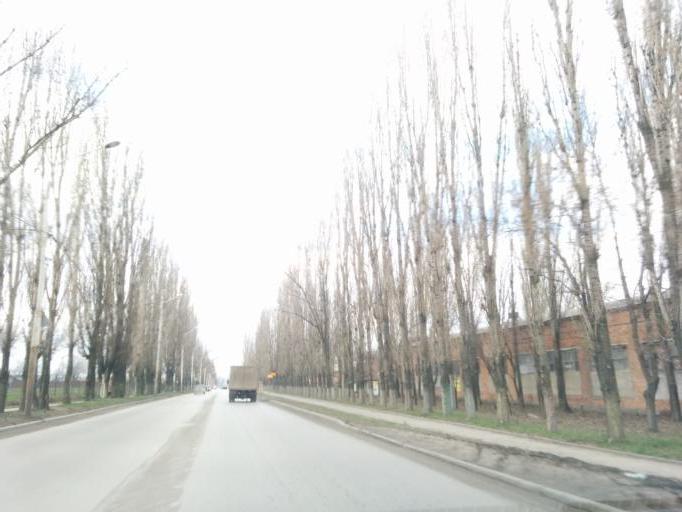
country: RU
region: Rostov
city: Shakhty
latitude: 47.6912
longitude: 40.2522
